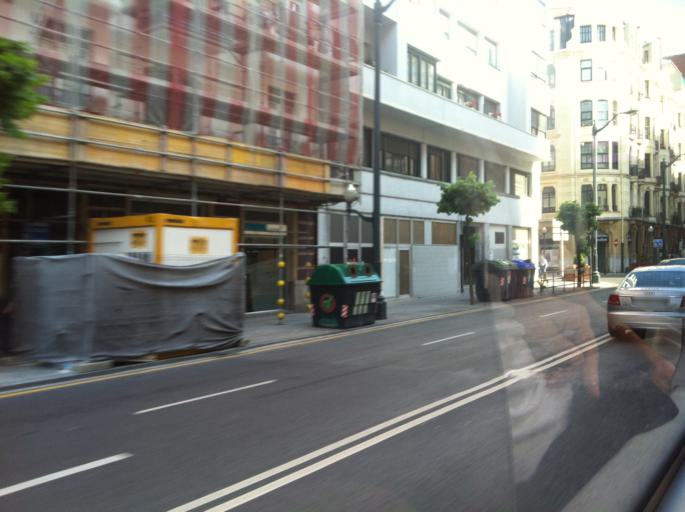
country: ES
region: Basque Country
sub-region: Bizkaia
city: Bilbao
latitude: 43.2674
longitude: -2.9332
